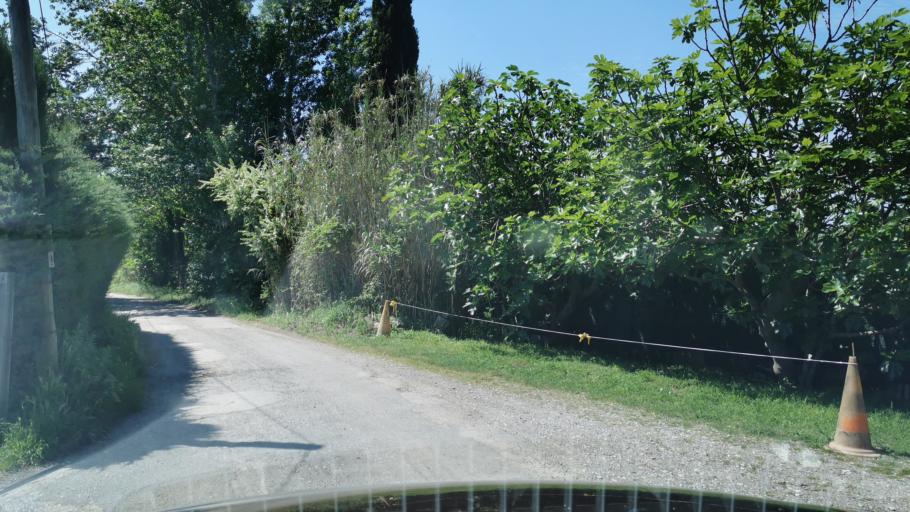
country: FR
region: Languedoc-Roussillon
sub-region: Departement de l'Aude
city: Narbonne
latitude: 43.1948
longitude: 3.0025
